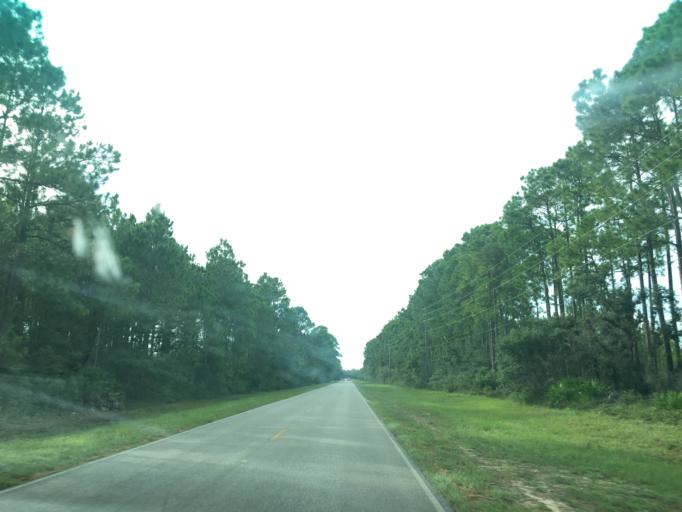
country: US
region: Florida
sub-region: Wakulla County
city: Crawfordville
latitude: 29.9380
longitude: -84.3811
